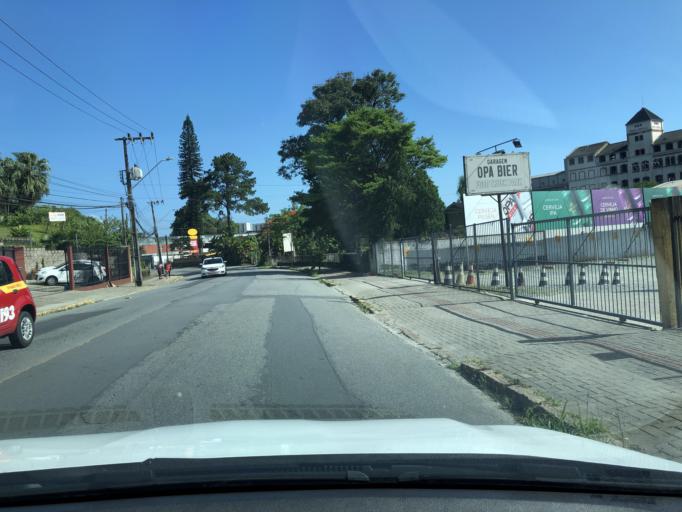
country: BR
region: Santa Catarina
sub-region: Joinville
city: Joinville
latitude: -26.3055
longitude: -48.8378
